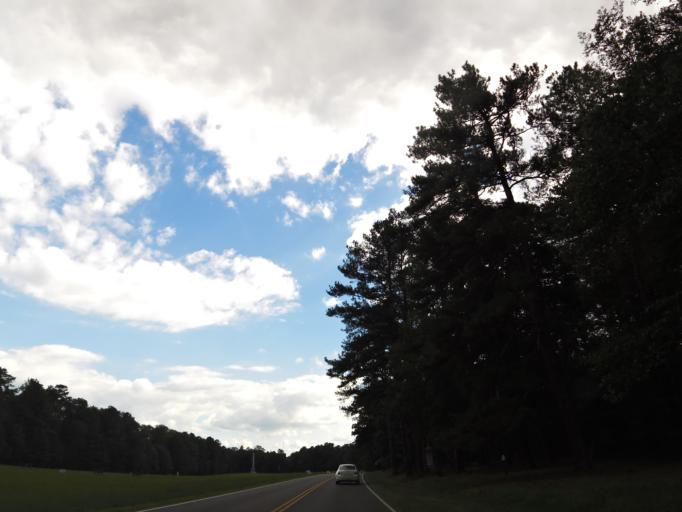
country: US
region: Georgia
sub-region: Catoosa County
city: Fort Oglethorpe
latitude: 34.9257
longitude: -85.2601
